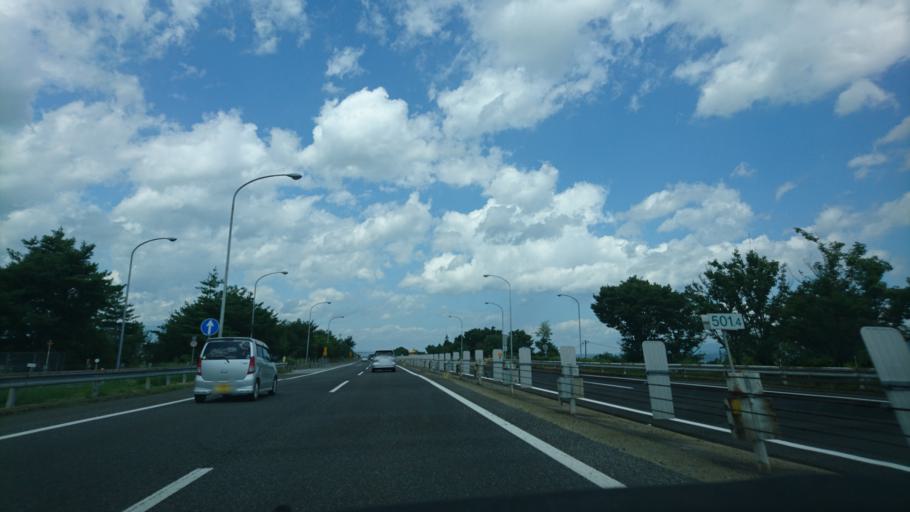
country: JP
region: Iwate
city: Morioka-shi
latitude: 39.6200
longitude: 141.1299
